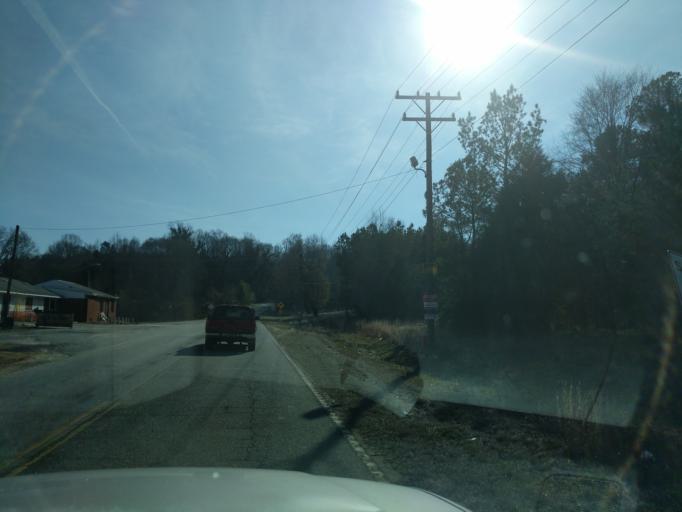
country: US
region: South Carolina
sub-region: Spartanburg County
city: Woodruff
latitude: 34.6499
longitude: -81.9641
